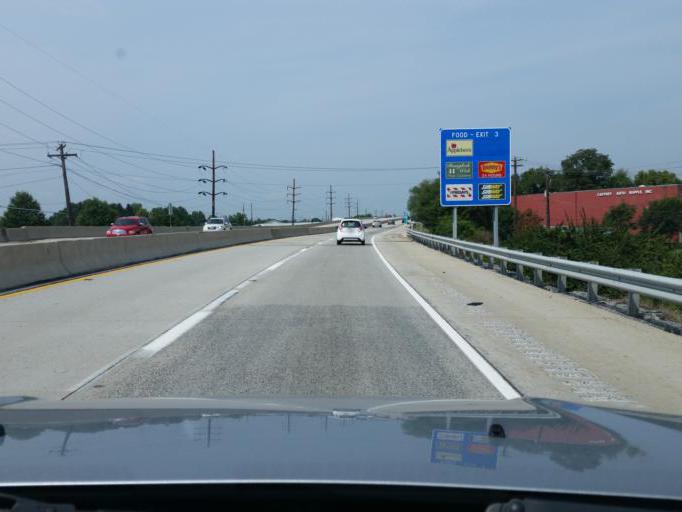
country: US
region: Pennsylvania
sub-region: Cumberland County
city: Shiremanstown
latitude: 40.2349
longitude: -76.9711
